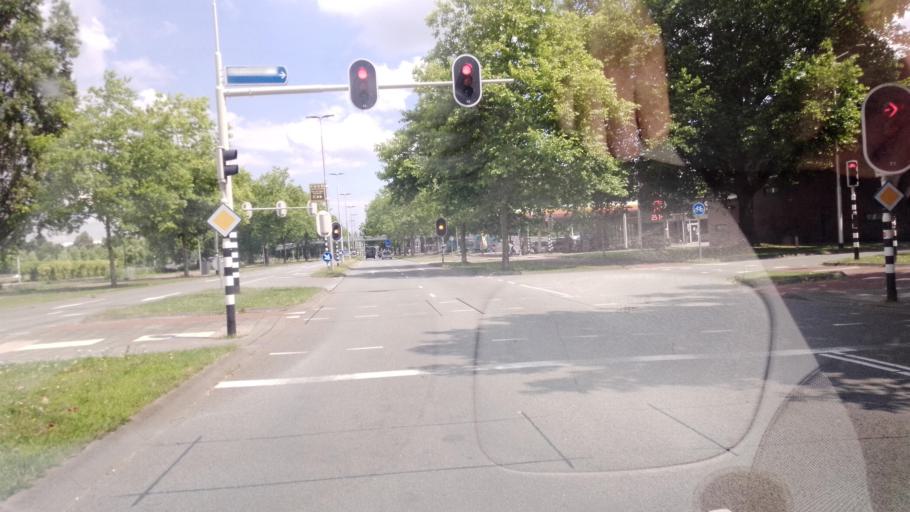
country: NL
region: Gelderland
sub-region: Gemeente Rozendaal
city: Rozendaal
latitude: 51.9834
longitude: 5.9467
